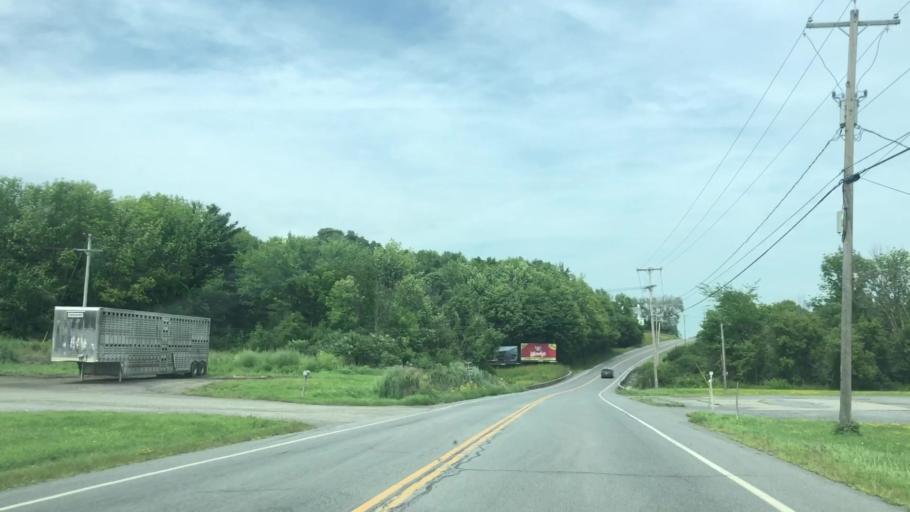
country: US
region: New York
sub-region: Washington County
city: Whitehall
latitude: 43.5271
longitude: -73.4137
